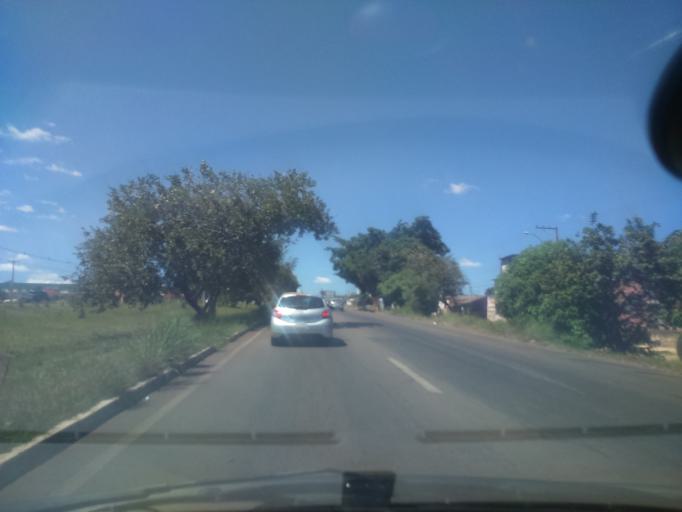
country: BR
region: Goias
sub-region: Luziania
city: Luziania
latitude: -16.0492
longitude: -48.0106
